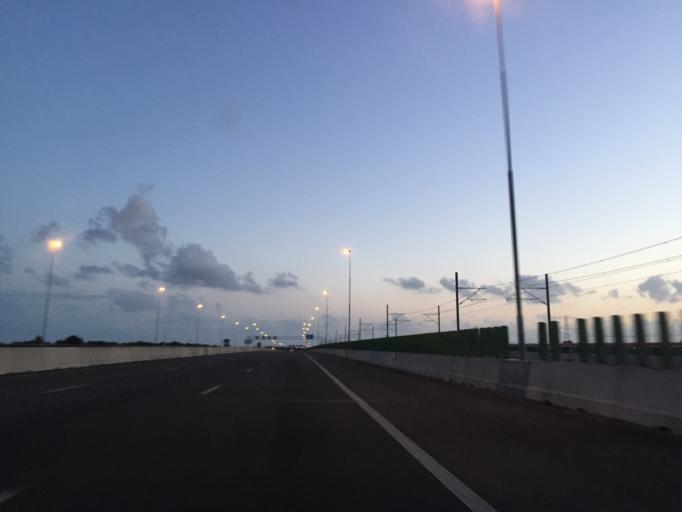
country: NL
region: North Holland
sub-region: Gemeente Naarden
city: Naarden
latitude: 52.3267
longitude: 5.1406
